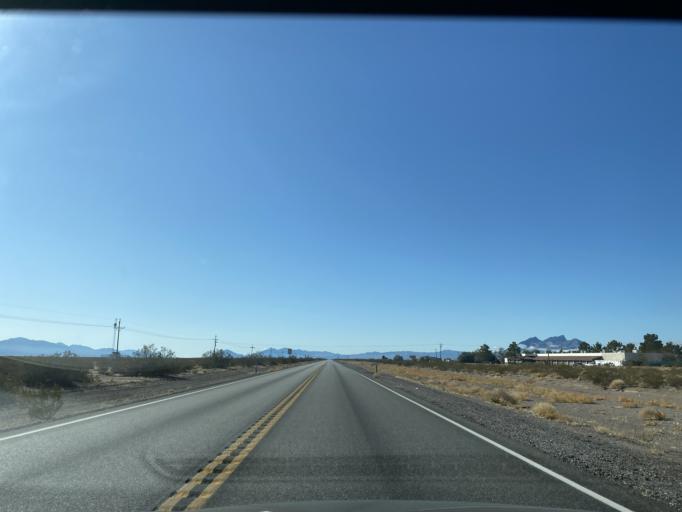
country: US
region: Nevada
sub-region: Nye County
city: Pahrump
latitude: 36.4977
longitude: -116.4214
